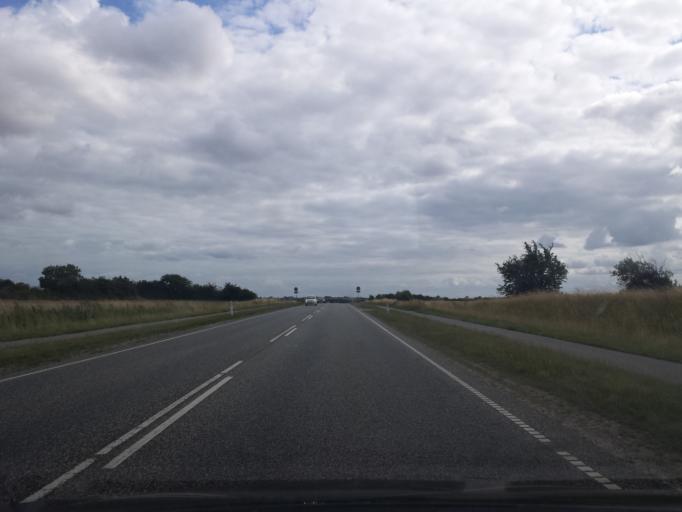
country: DK
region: South Denmark
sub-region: Sonderborg Kommune
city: Augustenborg
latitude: 54.9616
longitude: 9.8995
